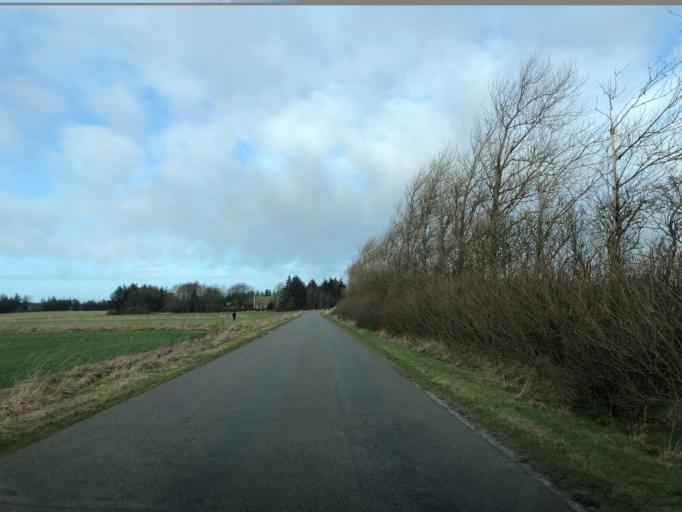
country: DK
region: Central Jutland
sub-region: Holstebro Kommune
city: Ulfborg
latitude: 56.3048
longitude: 8.2101
